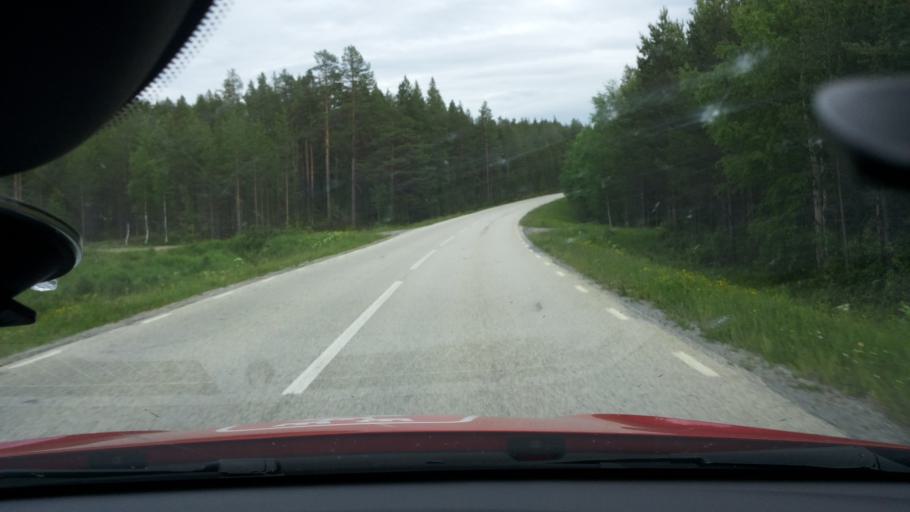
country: SE
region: Jaemtland
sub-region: Bergs Kommun
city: Hoverberg
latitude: 62.6998
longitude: 14.2609
